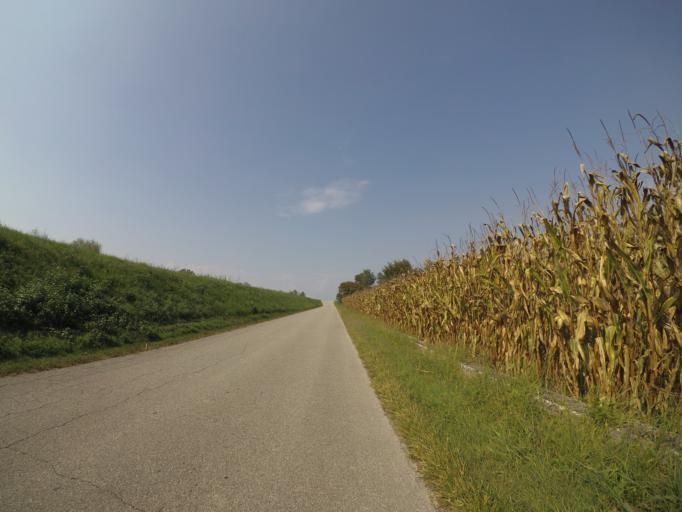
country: IT
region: Friuli Venezia Giulia
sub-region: Provincia di Udine
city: Camino al Tagliamento
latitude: 45.9045
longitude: 12.9362
